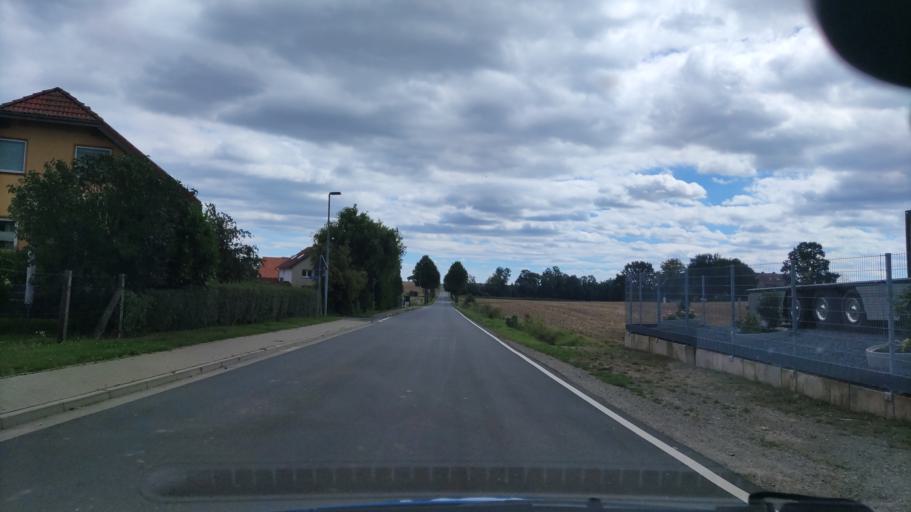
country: DE
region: Lower Saxony
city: Wangelnstedt
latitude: 51.8436
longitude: 9.7248
